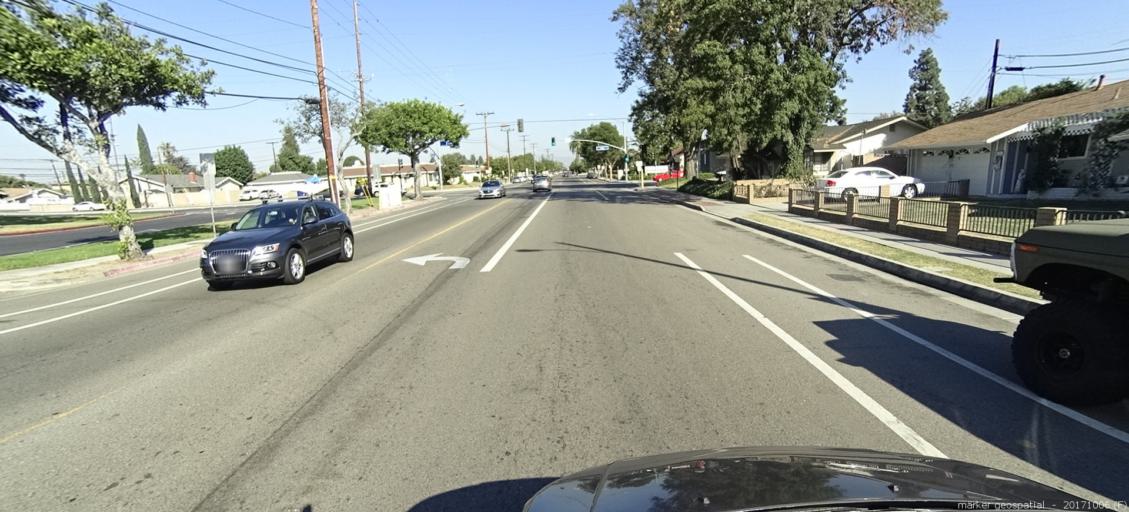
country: US
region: California
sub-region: Orange County
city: Stanton
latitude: 33.7811
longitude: -117.9848
